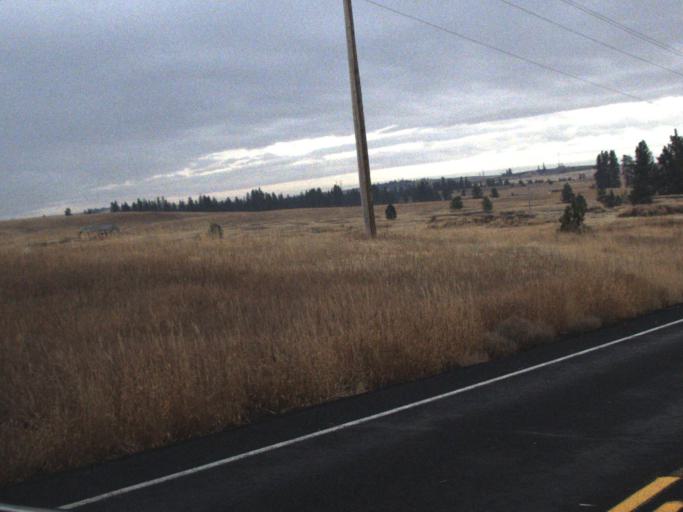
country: US
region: Washington
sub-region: Lincoln County
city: Davenport
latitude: 47.7620
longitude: -118.1735
